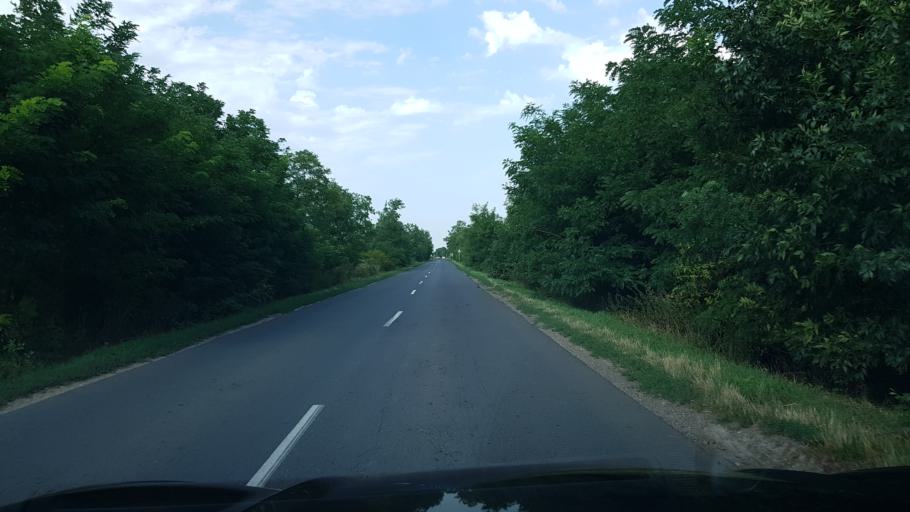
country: HU
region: Bekes
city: Fuzesgyarmat
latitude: 47.0824
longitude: 21.1966
